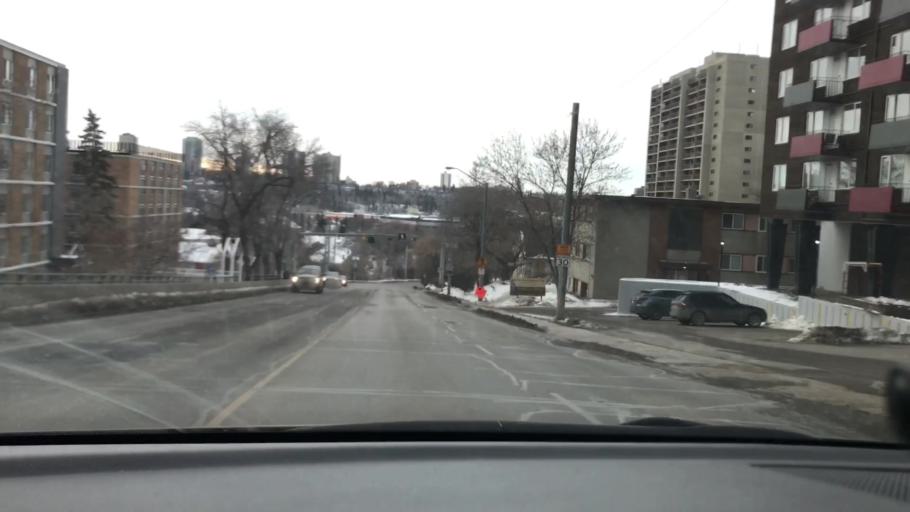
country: CA
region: Alberta
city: Edmonton
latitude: 53.5382
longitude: -113.4957
